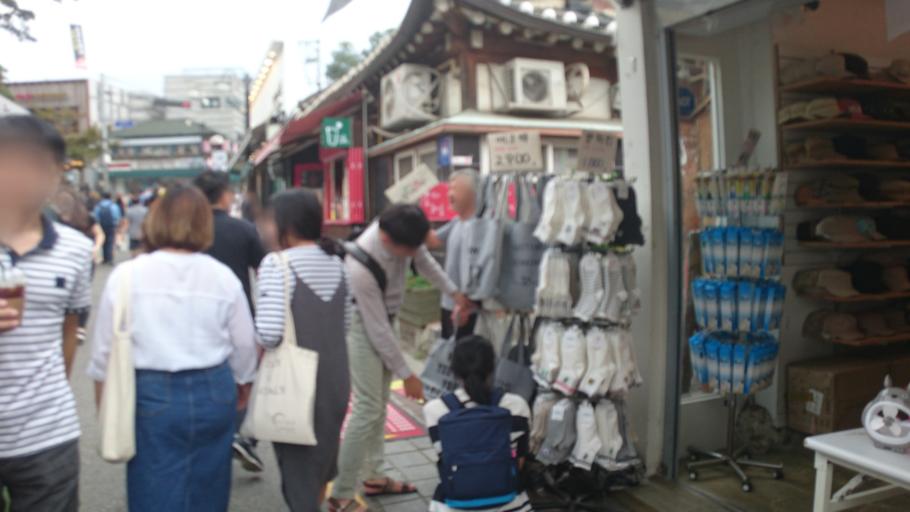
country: KR
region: Seoul
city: Seoul
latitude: 37.5791
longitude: 126.9822
